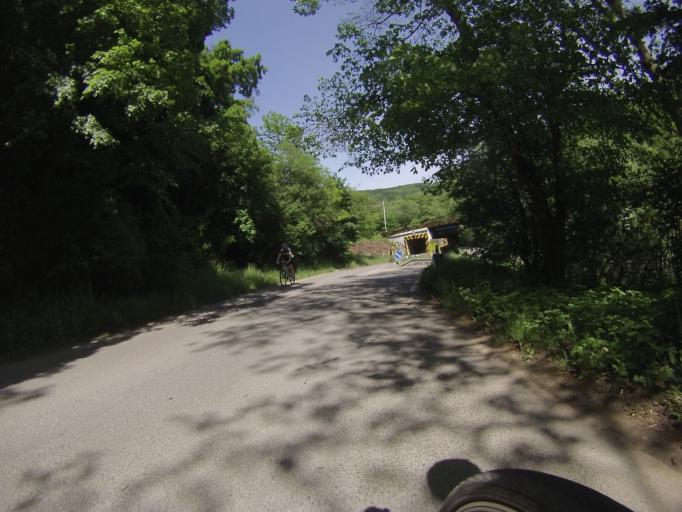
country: CZ
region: South Moravian
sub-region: Okres Blansko
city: Adamov
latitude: 49.2875
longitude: 16.6680
